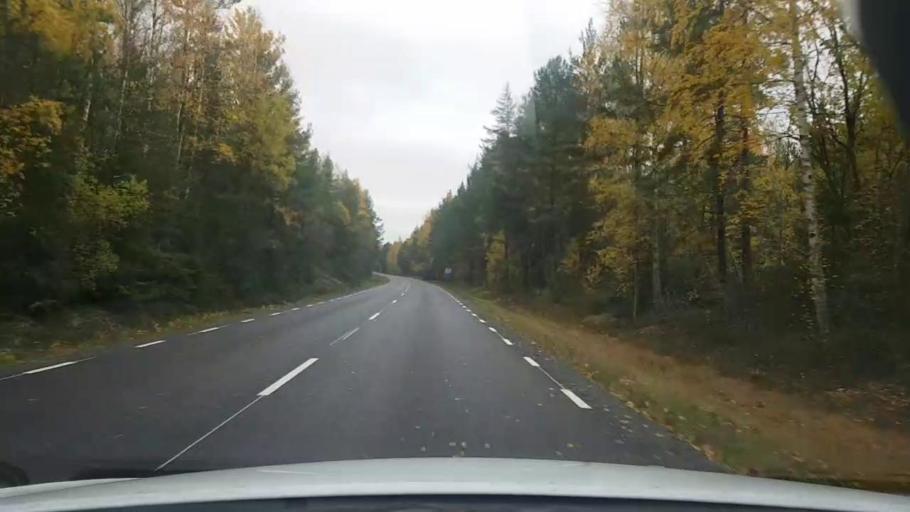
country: SE
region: OErebro
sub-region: Laxa Kommun
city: Laxa
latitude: 58.8030
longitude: 14.5427
